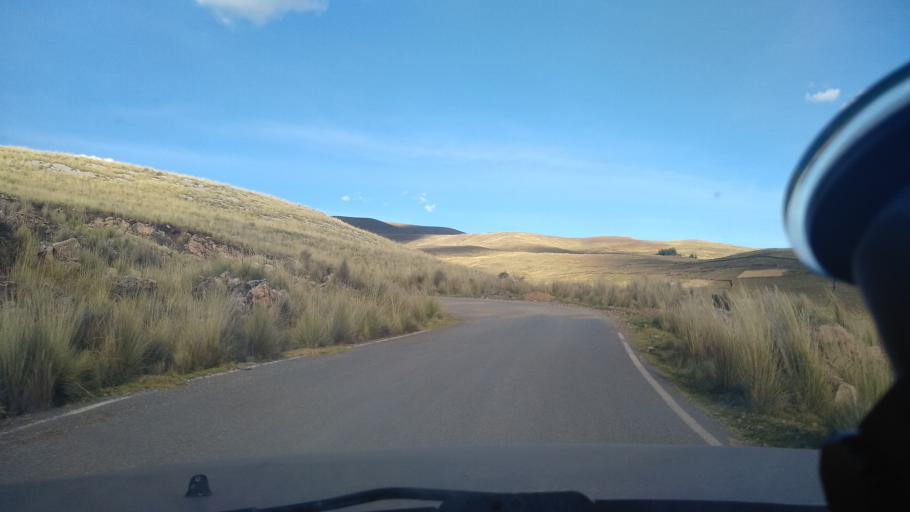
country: PE
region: Cusco
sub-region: Provincia de Canas
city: Cahuanuyo
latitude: -14.3427
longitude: -71.4461
